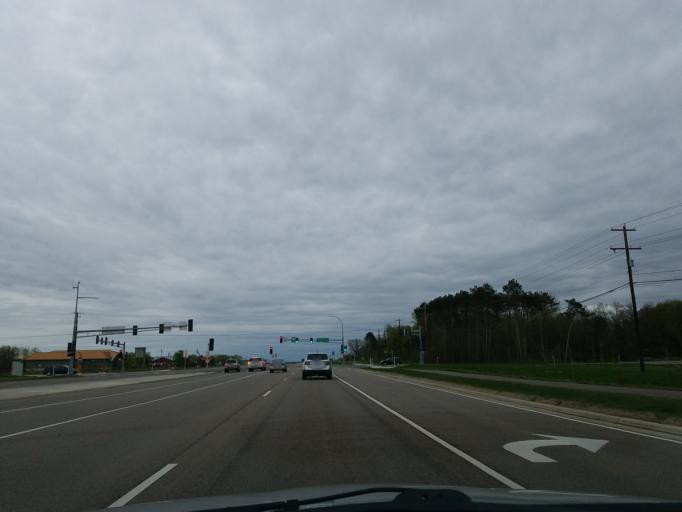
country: US
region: Minnesota
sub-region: Washington County
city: Stillwater
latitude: 45.0359
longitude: -92.8225
